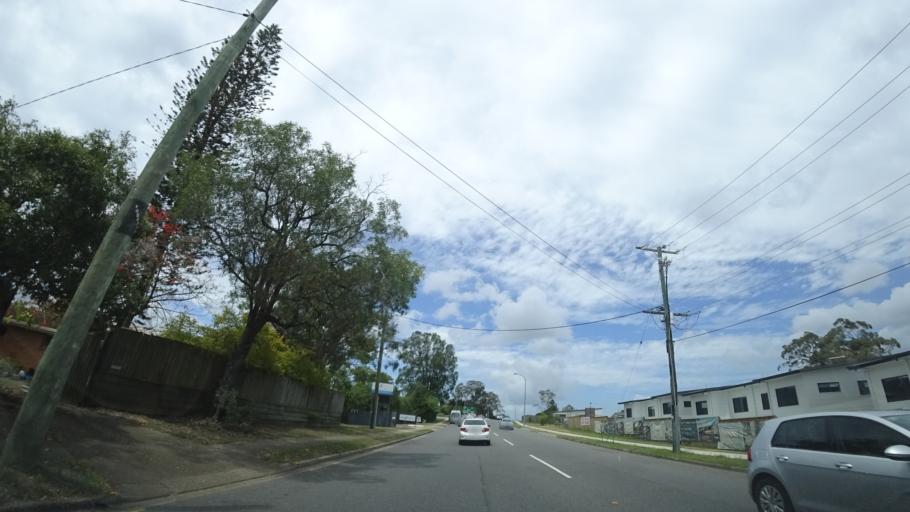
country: AU
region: Queensland
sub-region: Brisbane
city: Everton Park
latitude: -27.3870
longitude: 152.9818
